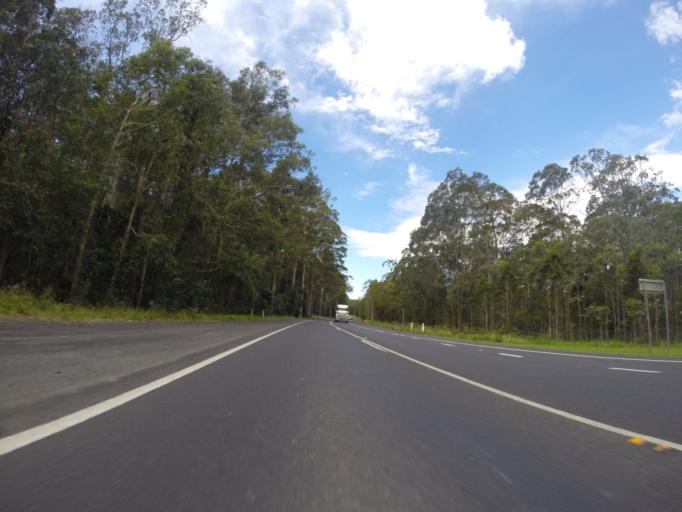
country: AU
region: New South Wales
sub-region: Shoalhaven Shire
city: Falls Creek
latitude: -35.0852
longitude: 150.5335
